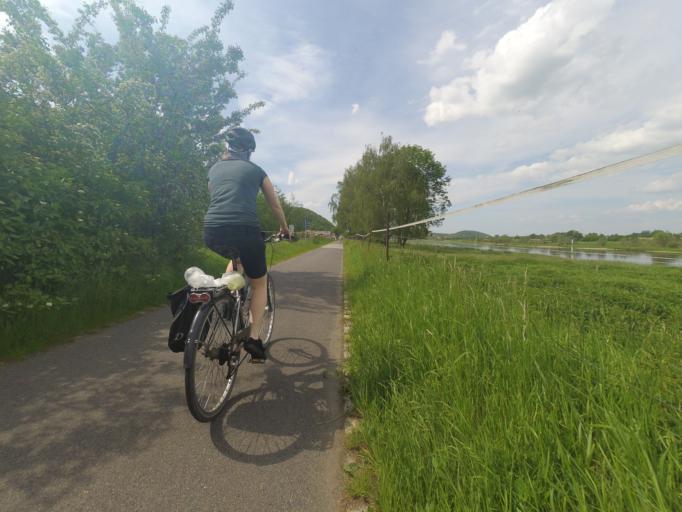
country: DE
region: Saxony
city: Klipphausen
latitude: 51.1235
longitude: 13.5366
